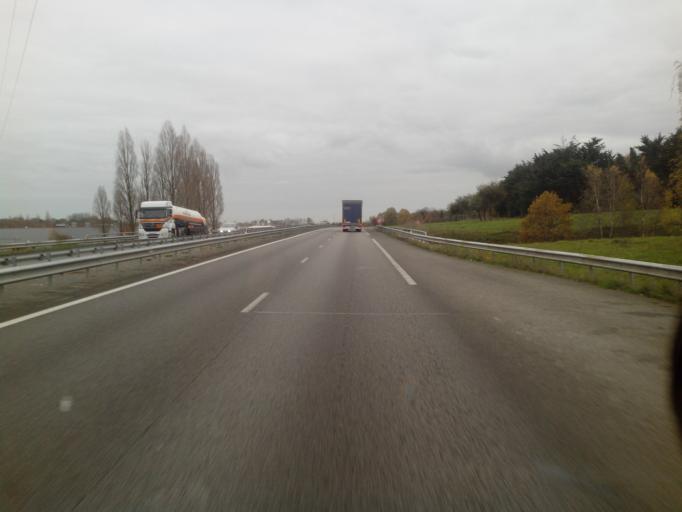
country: FR
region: Brittany
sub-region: Departement d'Ille-et-Vilaine
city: Laille
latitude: 47.9750
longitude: -1.6945
